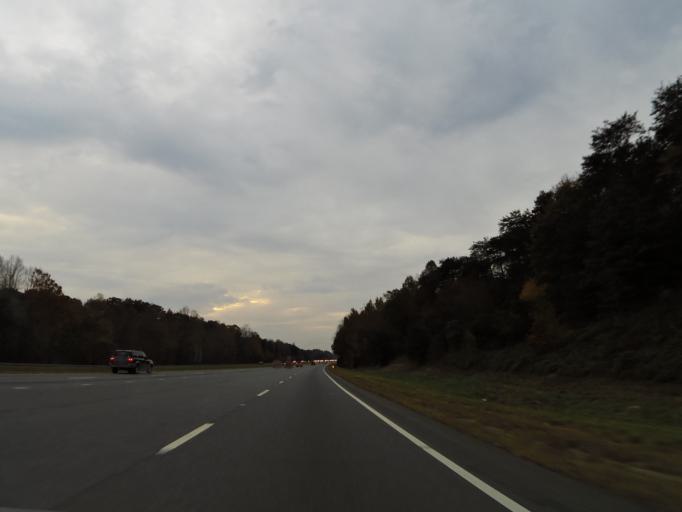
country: US
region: North Carolina
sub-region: Catawba County
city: Mountain View
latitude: 35.7075
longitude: -81.3621
